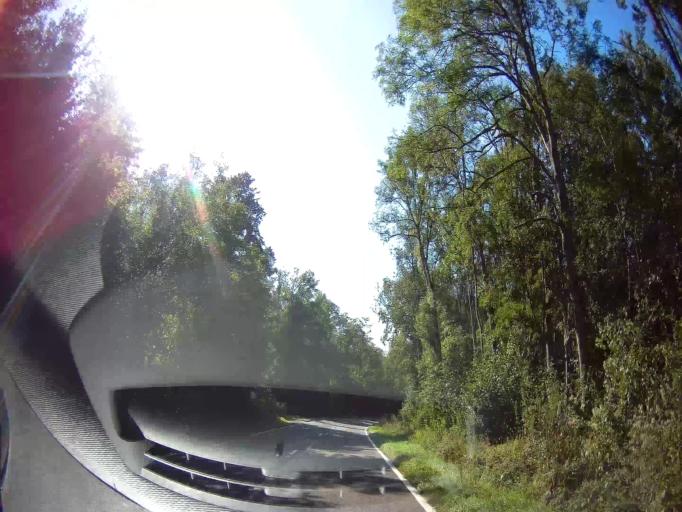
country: BE
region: Wallonia
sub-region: Province de Namur
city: Dinant
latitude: 50.2445
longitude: 4.9591
